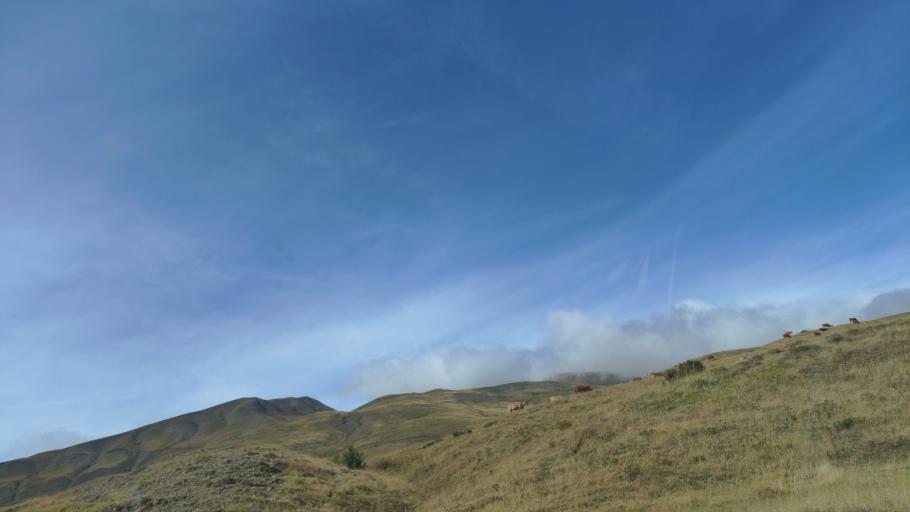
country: AL
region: Korce
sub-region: Rrethi i Kolonjes
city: Erseke
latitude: 40.3760
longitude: 20.8230
